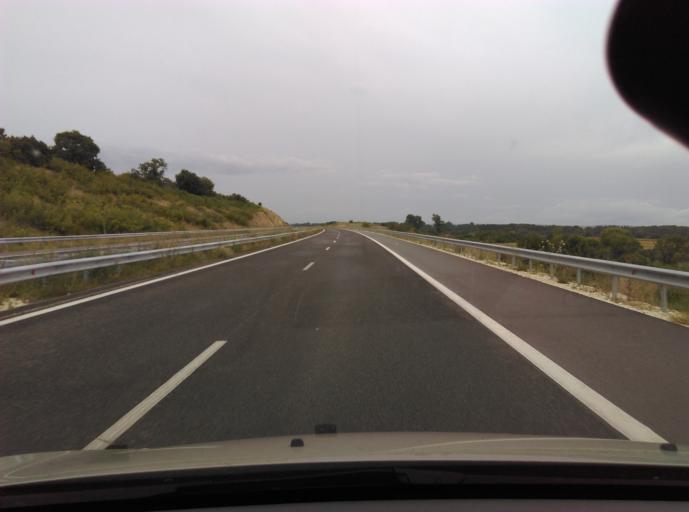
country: BG
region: Stara Zagora
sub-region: Obshtina Chirpan
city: Chirpan
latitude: 42.0990
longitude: 25.4283
